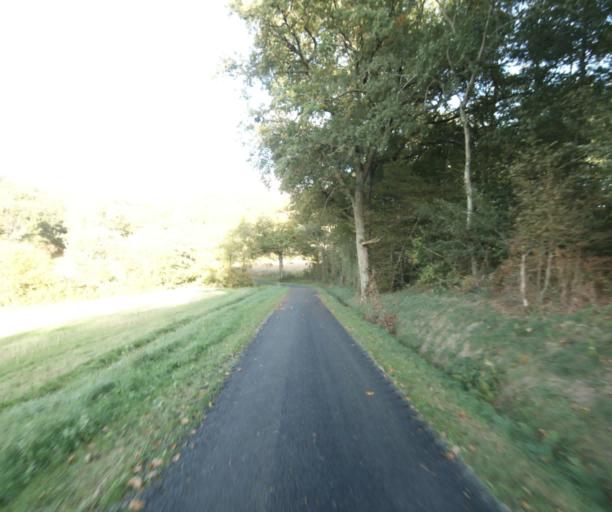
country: FR
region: Midi-Pyrenees
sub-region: Departement du Gers
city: Eauze
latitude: 43.7610
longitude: 0.0928
